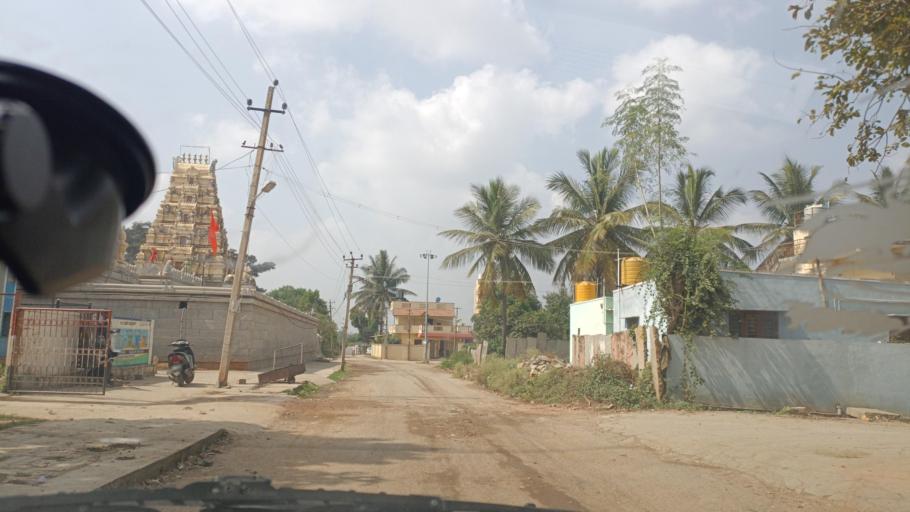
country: IN
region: Karnataka
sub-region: Bangalore Urban
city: Yelahanka
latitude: 13.1683
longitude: 77.6290
